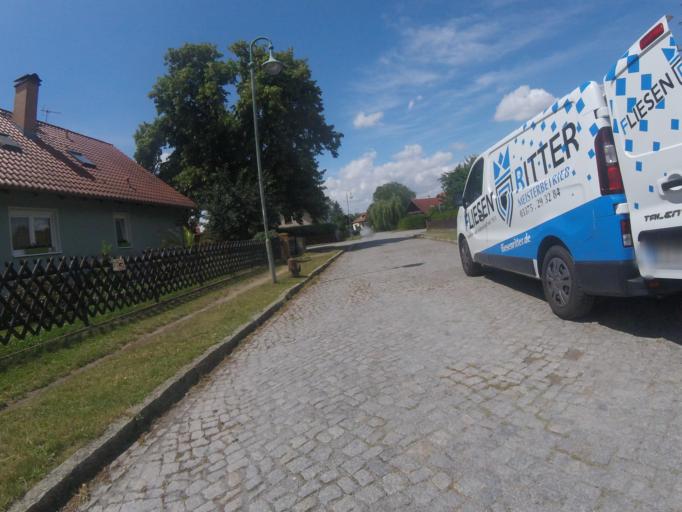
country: DE
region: Brandenburg
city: Konigs Wusterhausen
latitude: 52.2841
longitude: 13.6365
